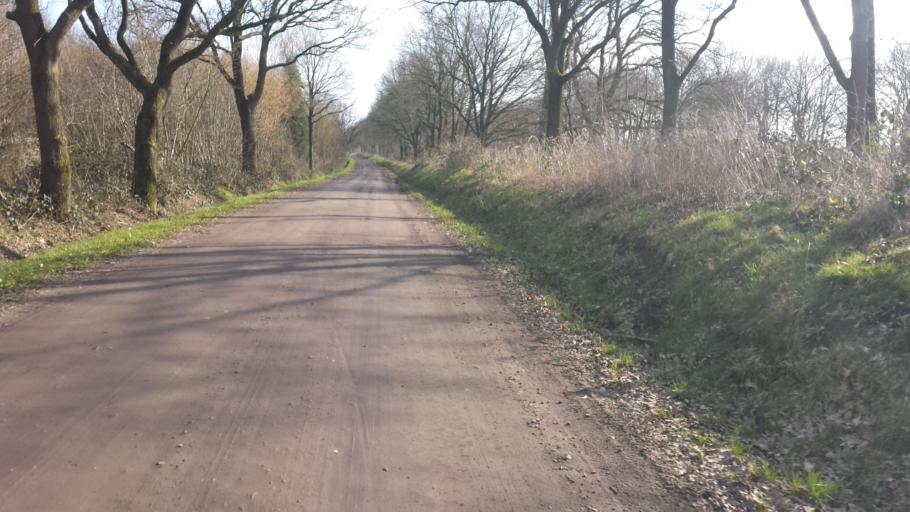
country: NL
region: Overijssel
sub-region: Gemeente Steenwijkerland
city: Tuk
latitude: 52.8095
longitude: 6.0853
